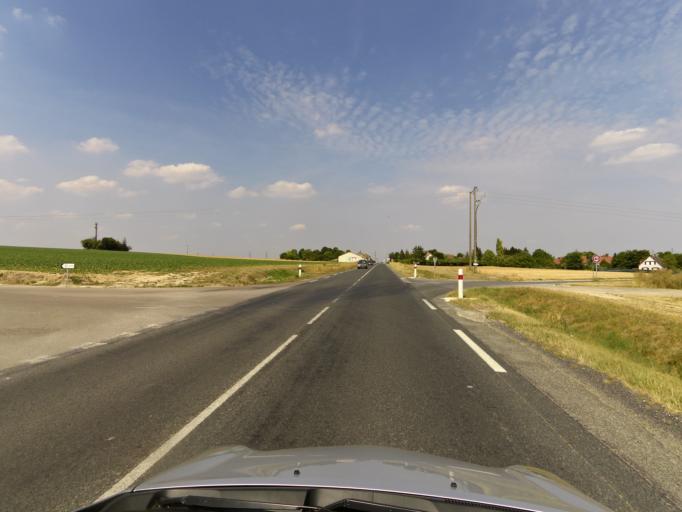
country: FR
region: Champagne-Ardenne
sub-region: Departement de la Marne
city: Bezannes
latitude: 49.1944
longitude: 4.0130
